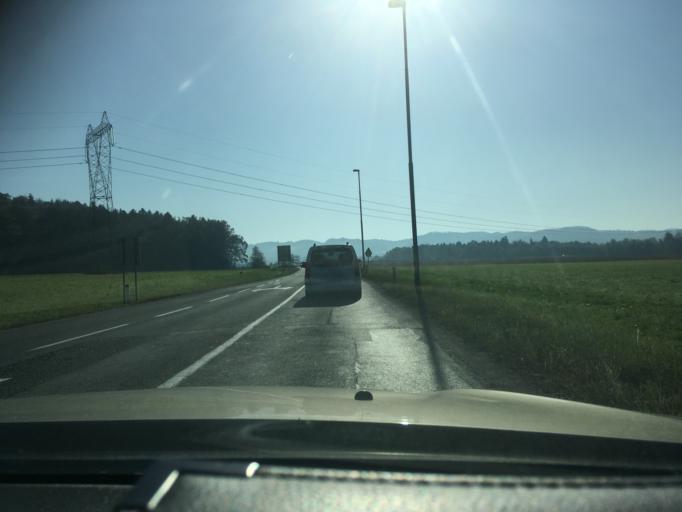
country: SI
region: Domzale
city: Dob
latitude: 46.1583
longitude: 14.6449
